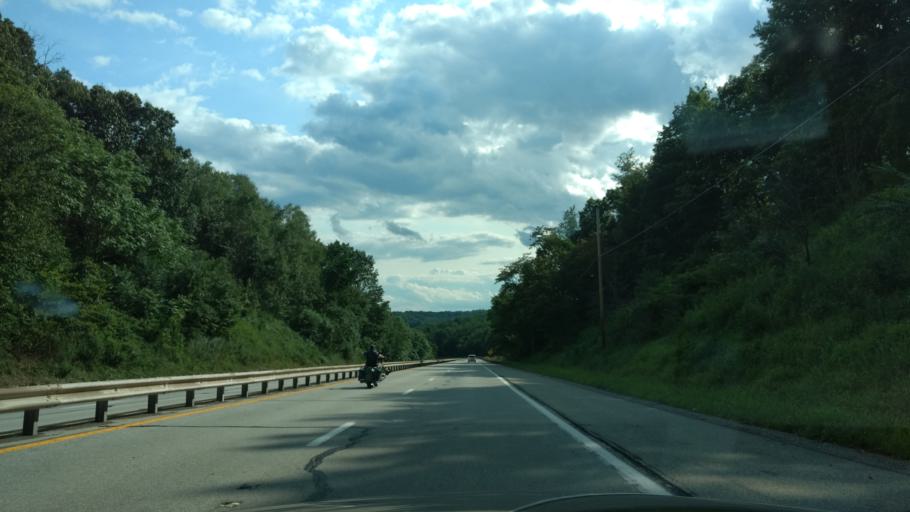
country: US
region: Pennsylvania
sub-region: Armstrong County
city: Apollo
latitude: 40.5201
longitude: -79.6404
